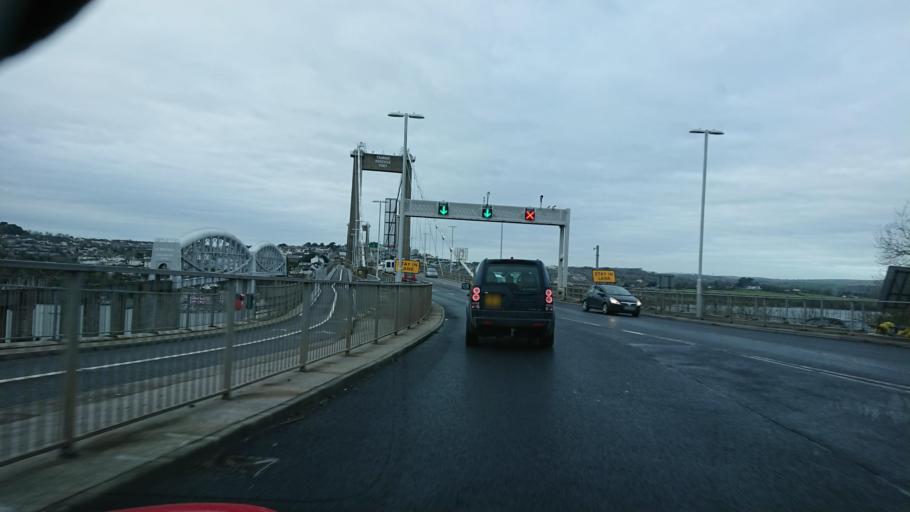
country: GB
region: England
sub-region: Cornwall
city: Saltash
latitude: 50.4077
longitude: -4.1986
